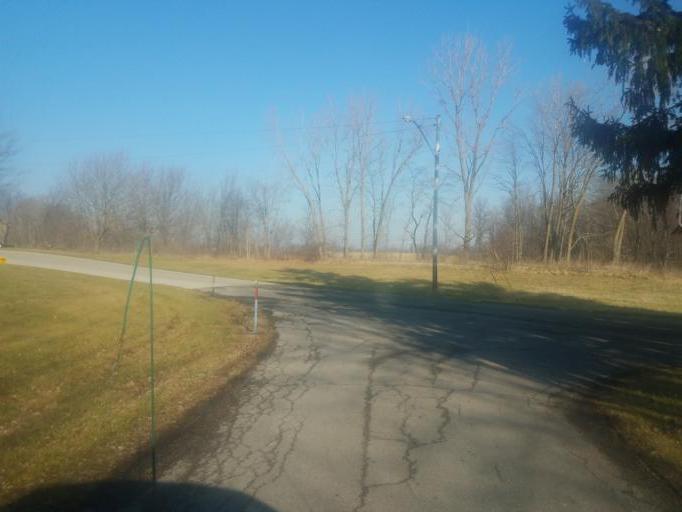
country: US
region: Ohio
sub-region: Seneca County
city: Tiffin
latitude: 41.0544
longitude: -83.0125
